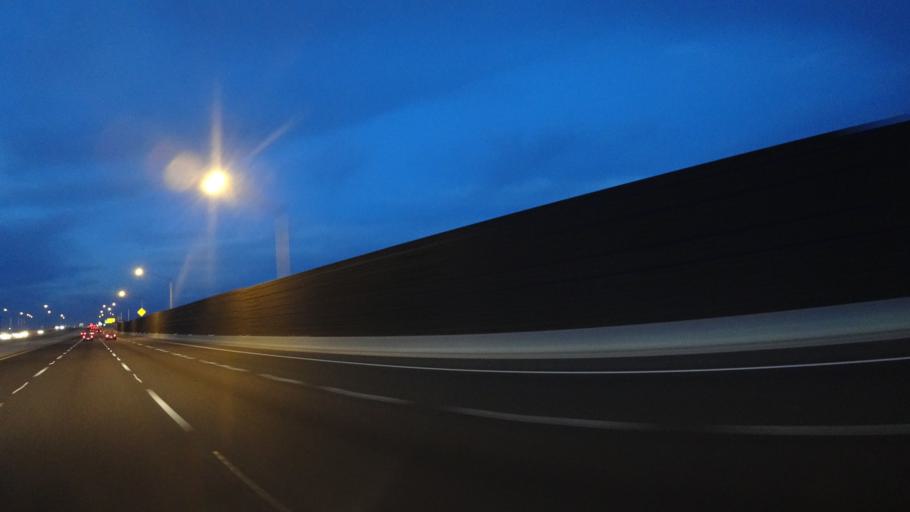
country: US
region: Arizona
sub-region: Maricopa County
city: Citrus Park
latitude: 33.5873
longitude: -112.4179
